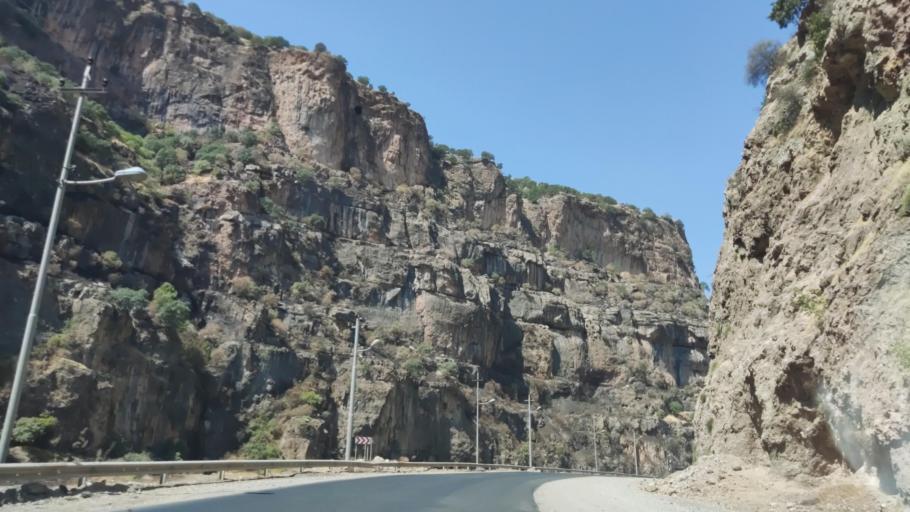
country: IQ
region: Arbil
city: Ruwandiz
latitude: 36.6267
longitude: 44.4631
